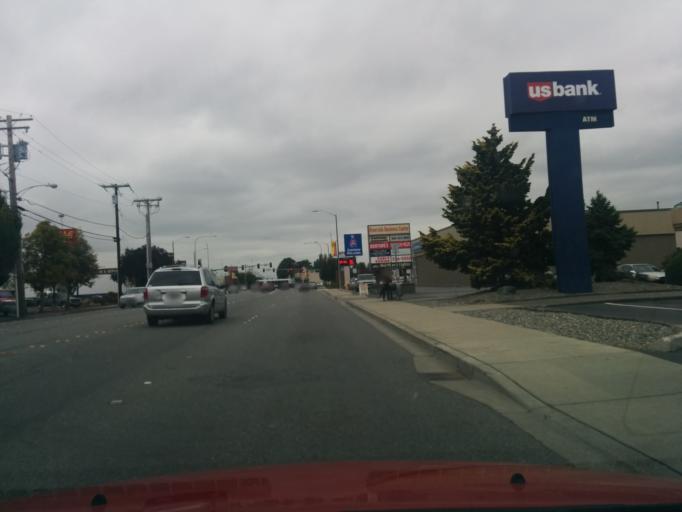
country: US
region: Washington
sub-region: Skagit County
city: Mount Vernon
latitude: 48.4341
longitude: -122.3351
